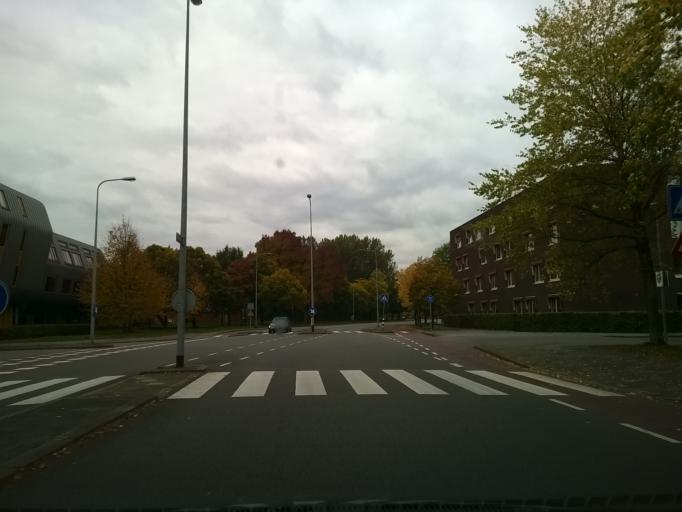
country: NL
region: Groningen
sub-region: Gemeente Groningen
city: Groningen
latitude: 53.2213
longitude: 6.5286
